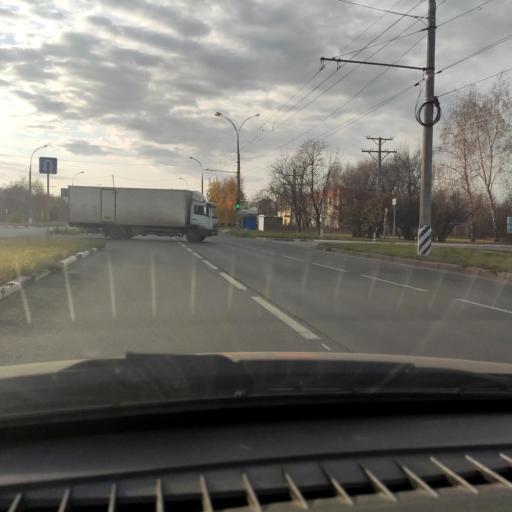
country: RU
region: Samara
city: Tol'yatti
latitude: 53.5439
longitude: 49.3009
